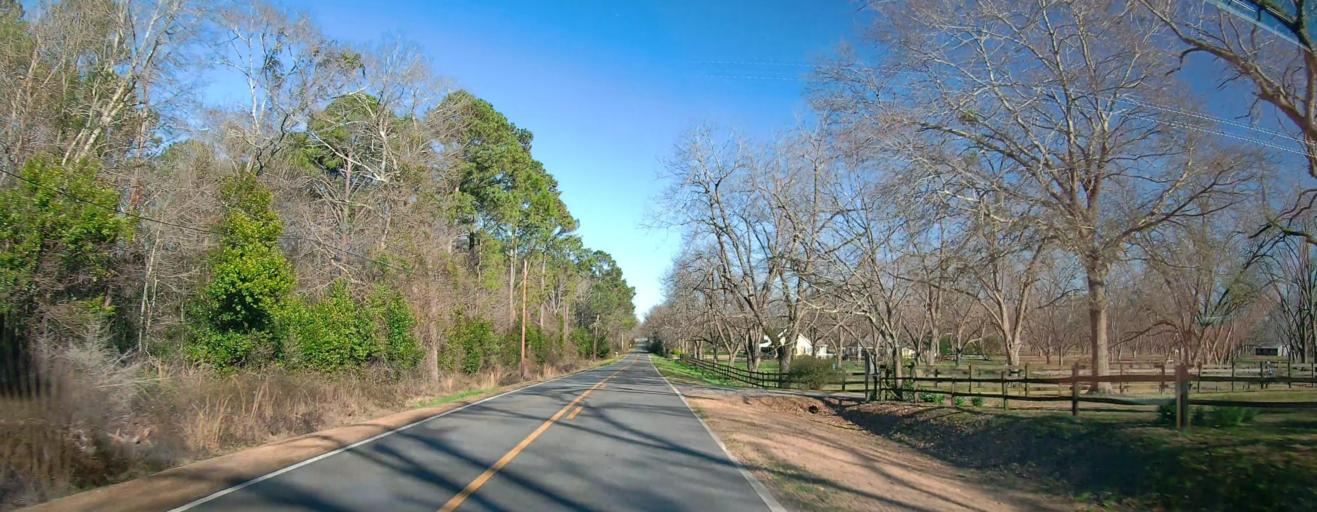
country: US
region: Georgia
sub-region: Sumter County
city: Americus
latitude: 32.0469
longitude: -84.2630
